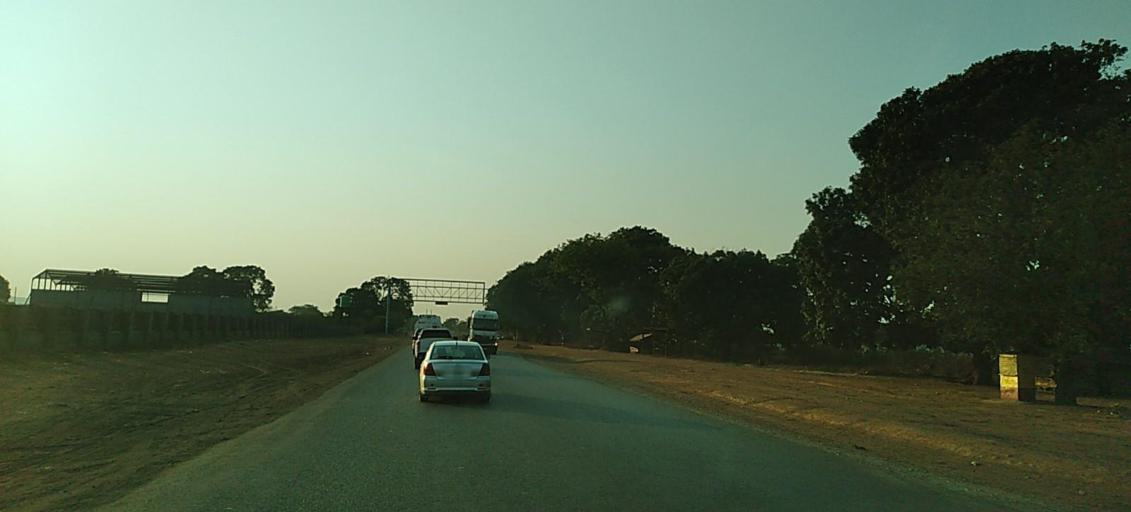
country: ZM
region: Copperbelt
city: Ndola
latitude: -13.0355
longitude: 28.6899
